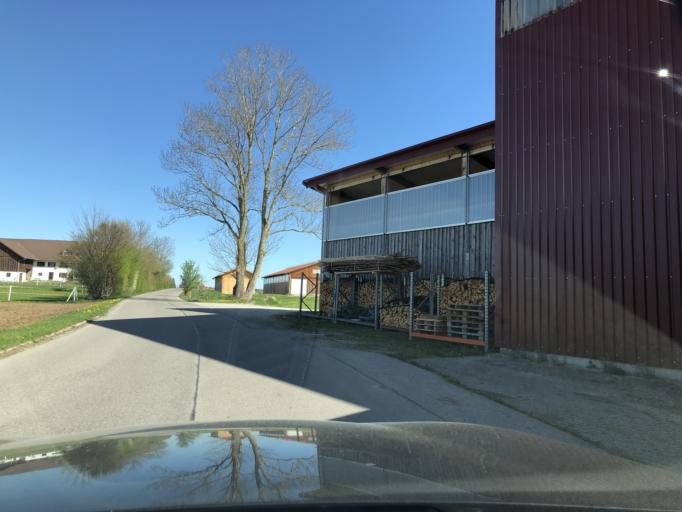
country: DE
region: Bavaria
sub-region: Swabia
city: Wald
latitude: 47.7559
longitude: 10.5695
